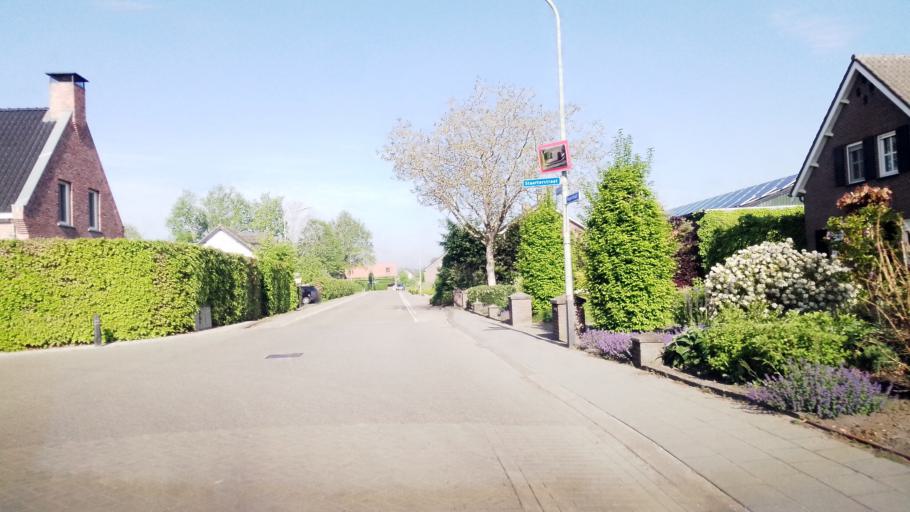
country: NL
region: Limburg
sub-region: Gemeente Peel en Maas
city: Maasbree
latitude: 51.4116
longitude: 6.0283
